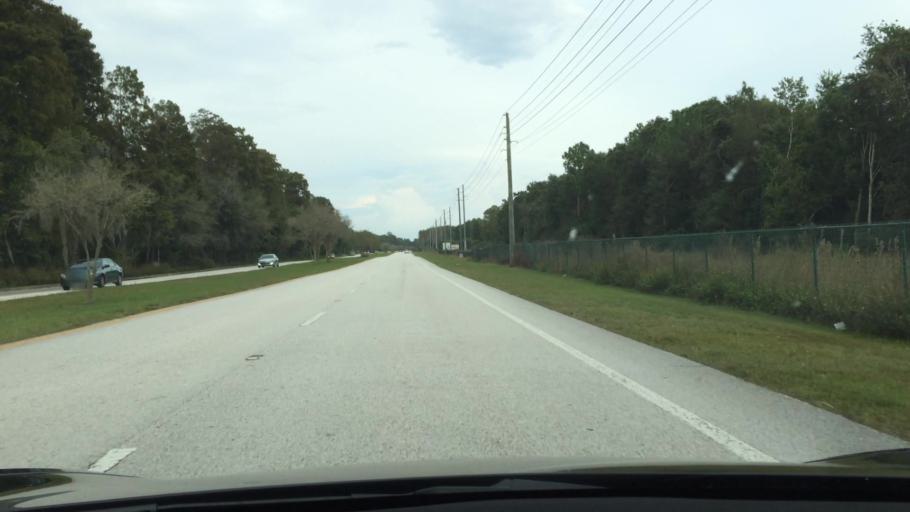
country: US
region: Florida
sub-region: Pasco County
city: Trinity
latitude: 28.1672
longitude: -82.6940
